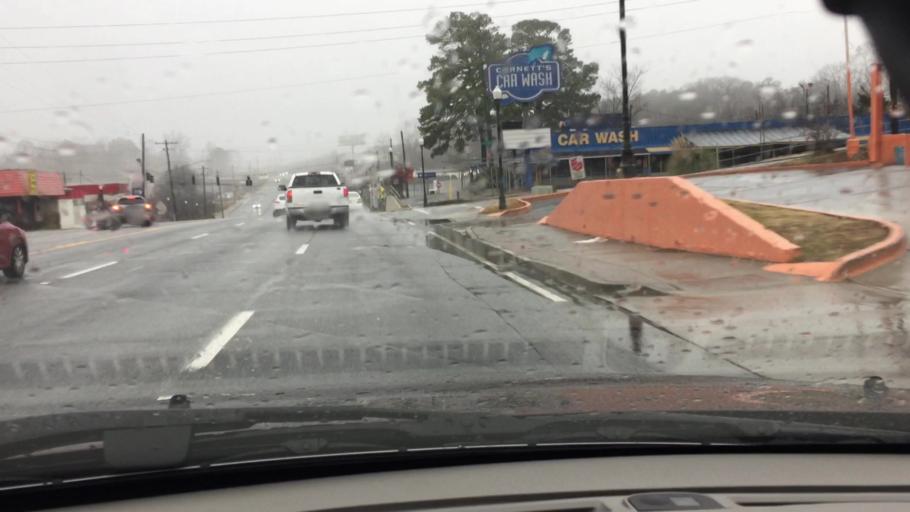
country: US
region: Georgia
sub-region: DeKalb County
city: Doraville
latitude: 33.9008
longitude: -84.2768
